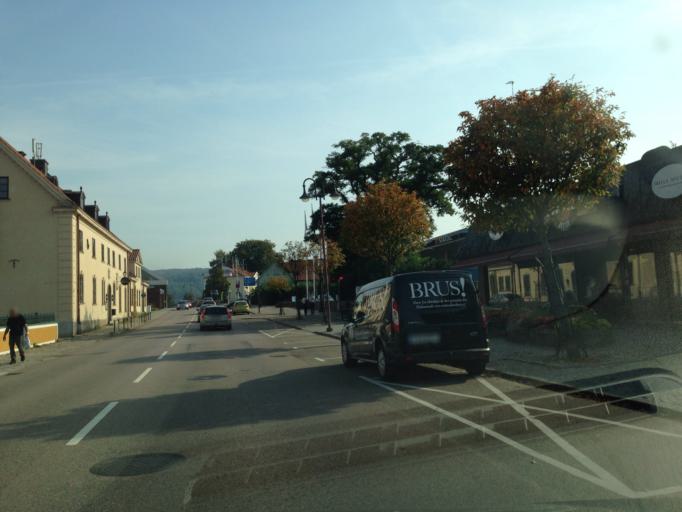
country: SE
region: Skane
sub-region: Bastads Kommun
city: Bastad
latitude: 56.4308
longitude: 12.8397
